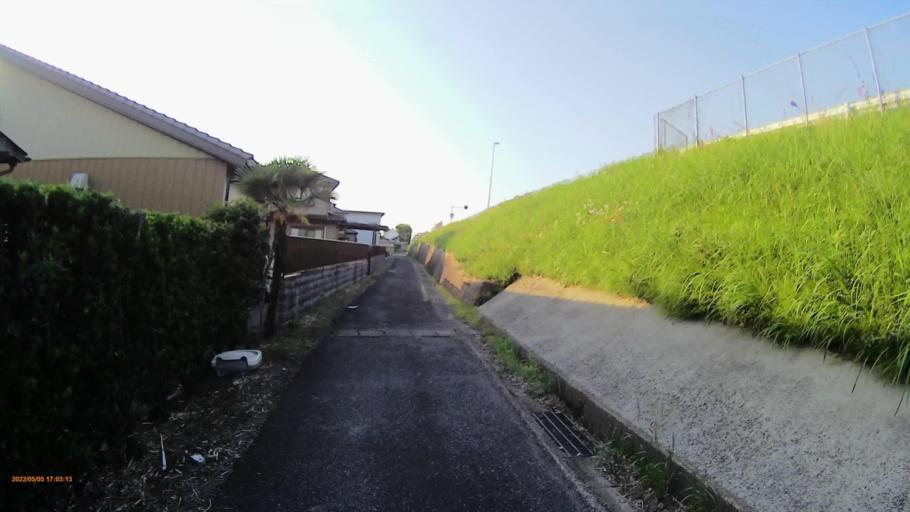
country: JP
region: Saitama
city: Kurihashi
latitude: 36.1177
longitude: 139.7196
